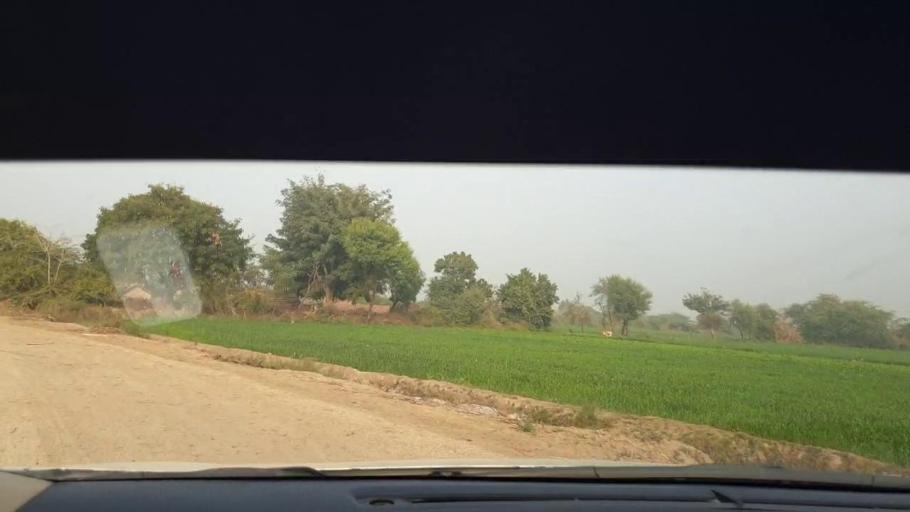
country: PK
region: Sindh
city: Berani
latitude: 25.8011
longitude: 68.8524
